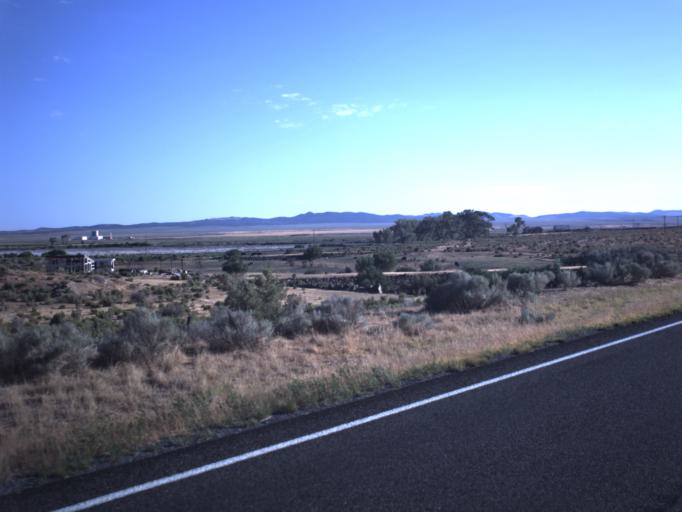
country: US
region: Utah
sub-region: Iron County
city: Enoch
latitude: 37.8514
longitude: -113.0345
